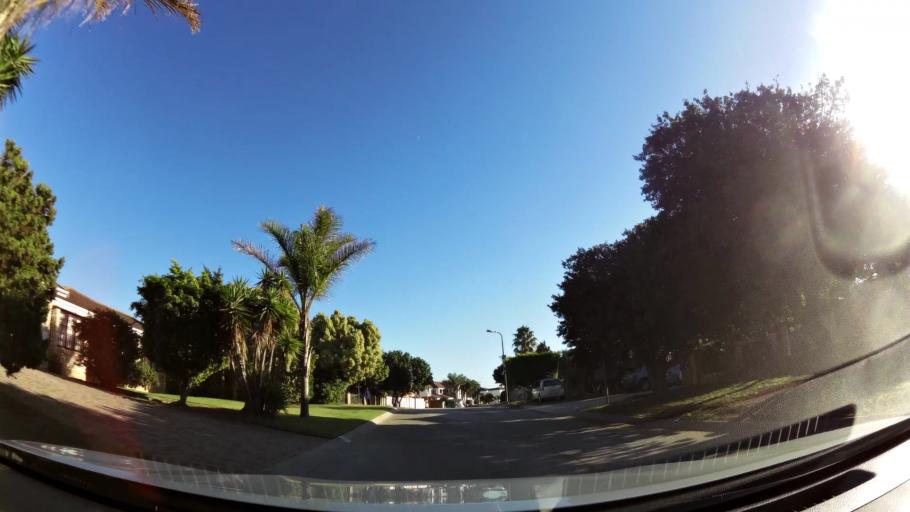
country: ZA
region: Eastern Cape
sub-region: Nelson Mandela Bay Metropolitan Municipality
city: Port Elizabeth
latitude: -33.9898
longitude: 25.6516
